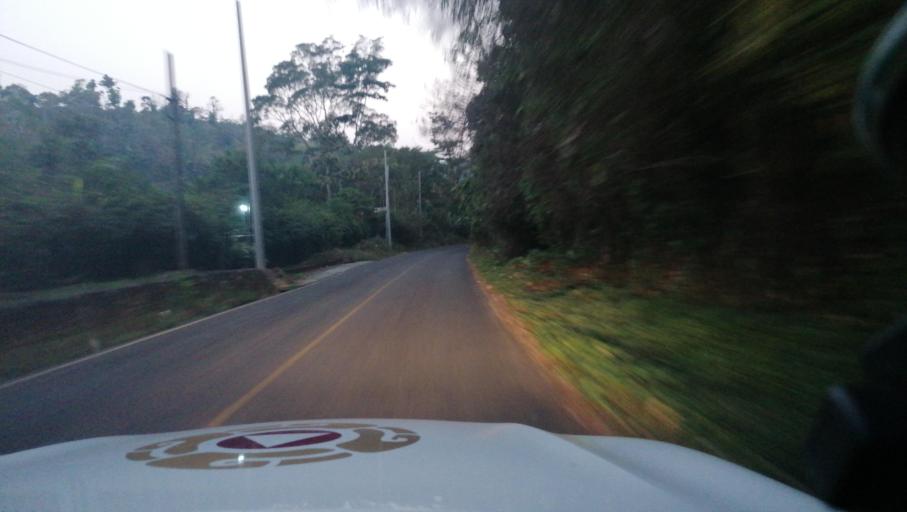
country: MX
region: Chiapas
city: Veinte de Noviembre
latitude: 14.9954
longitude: -92.2429
